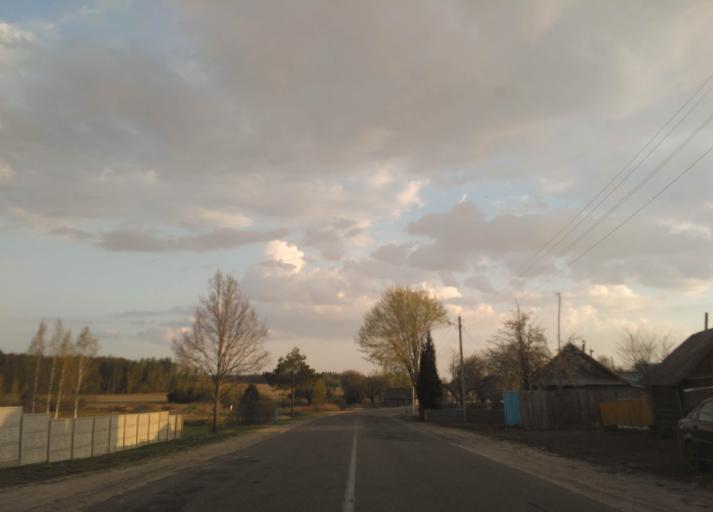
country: BY
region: Minsk
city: Loshnitsa
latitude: 54.4128
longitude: 28.6306
